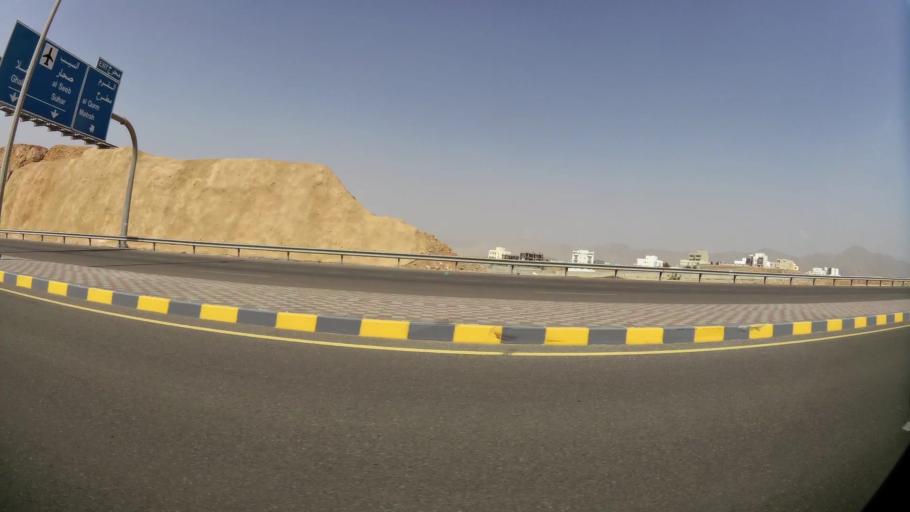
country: OM
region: Muhafazat Masqat
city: Bawshar
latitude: 23.5570
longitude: 58.3393
